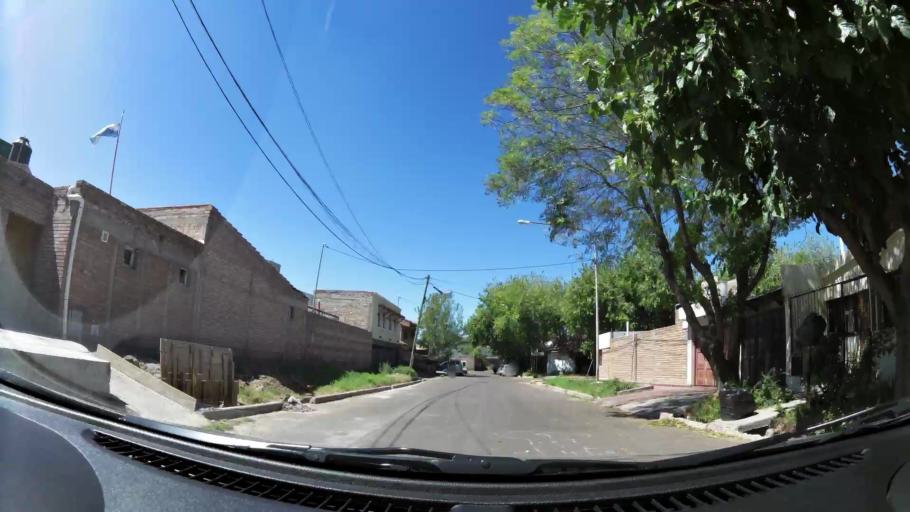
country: AR
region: Mendoza
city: Las Heras
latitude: -32.8536
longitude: -68.8485
